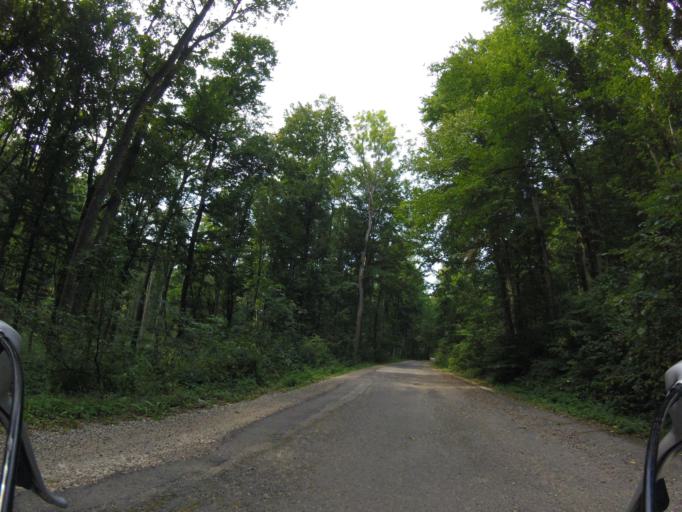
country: HU
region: Veszprem
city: Herend
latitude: 47.2048
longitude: 17.6652
